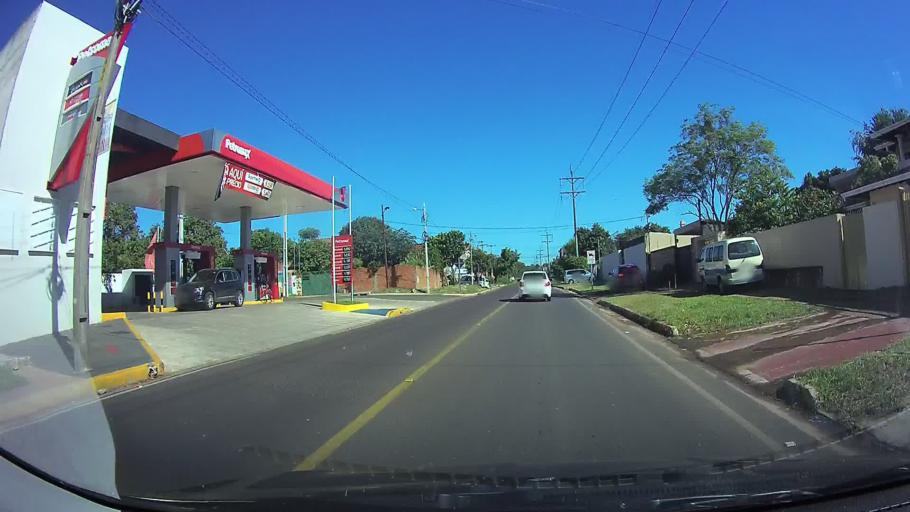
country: PY
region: Central
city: Fernando de la Mora
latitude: -25.3044
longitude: -57.5311
